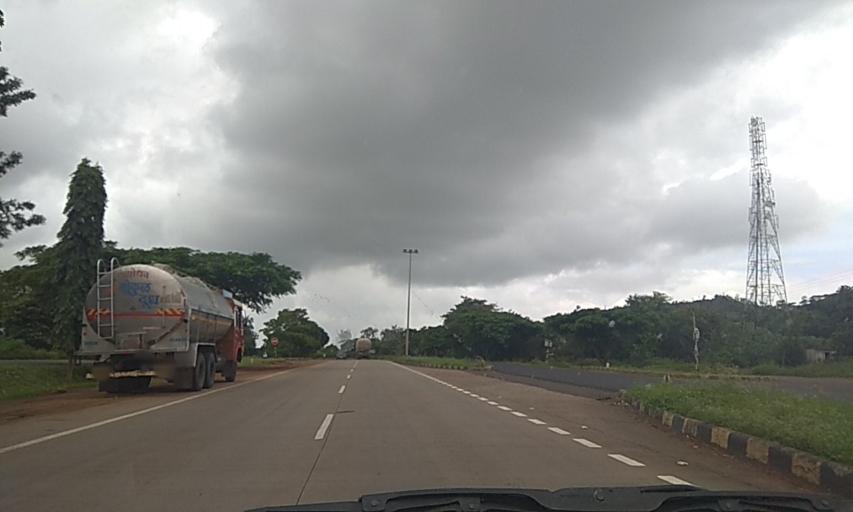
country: IN
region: Karnataka
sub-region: Belgaum
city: Sankeshwar
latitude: 16.2736
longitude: 74.4579
